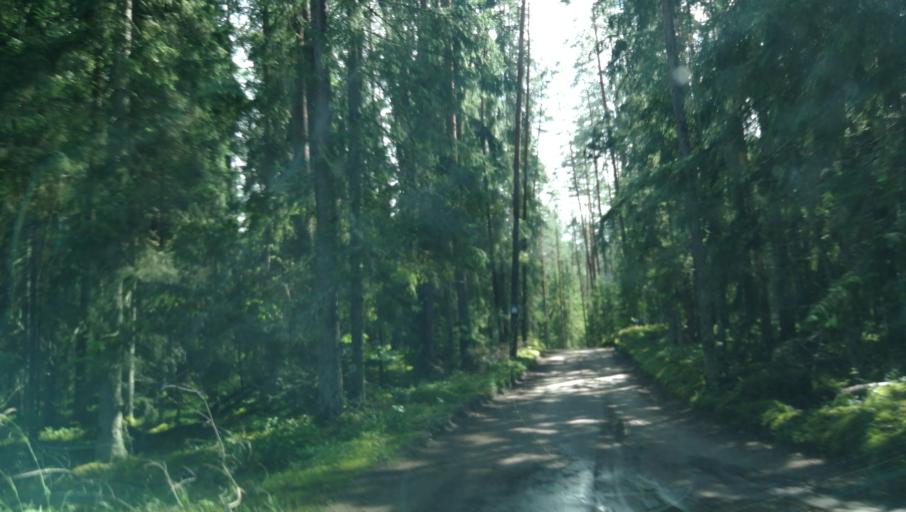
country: LV
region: Cesu Rajons
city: Cesis
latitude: 57.3024
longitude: 25.2096
